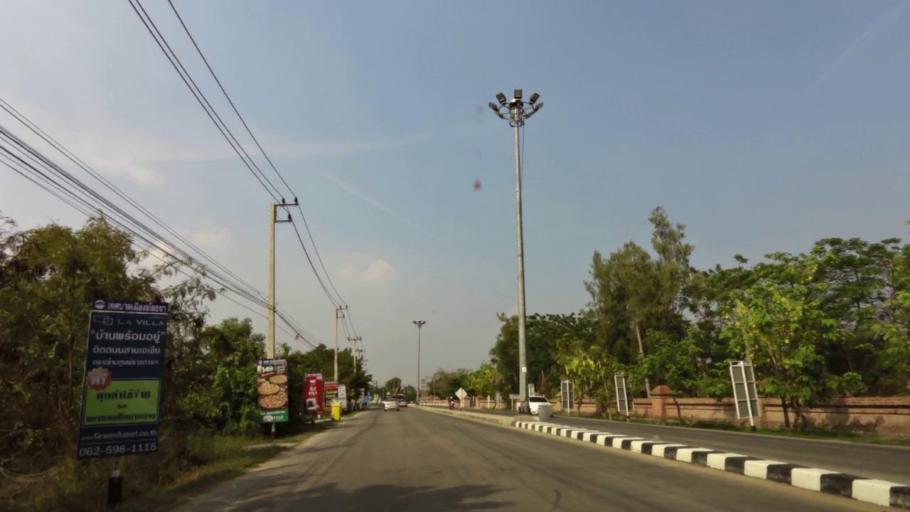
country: TH
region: Phra Nakhon Si Ayutthaya
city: Phra Nakhon Si Ayutthaya
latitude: 14.3428
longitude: 100.5916
